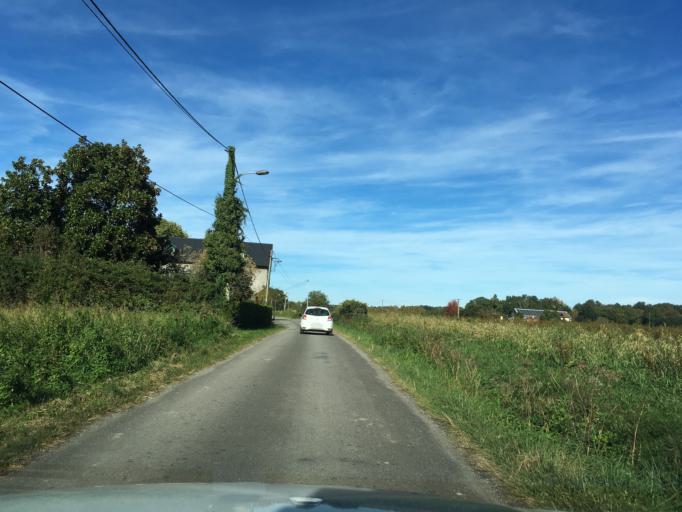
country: FR
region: Aquitaine
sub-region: Departement des Pyrenees-Atlantiques
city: Montardon
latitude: 43.3315
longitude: -0.3413
